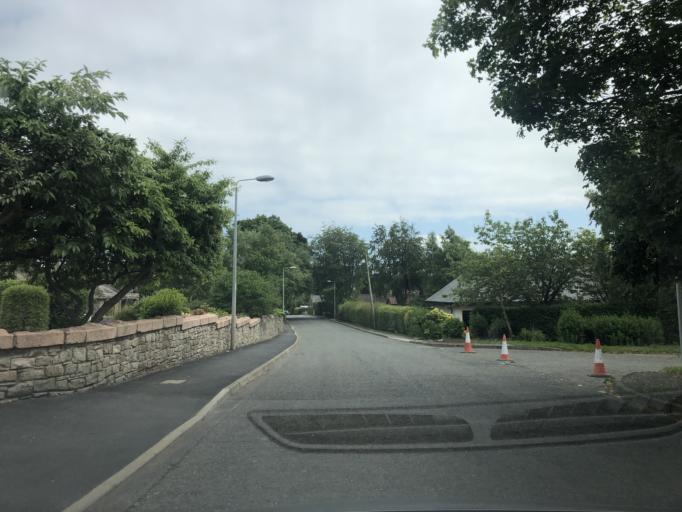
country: GB
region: Scotland
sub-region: Angus
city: Brechin
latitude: 56.7358
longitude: -2.6754
